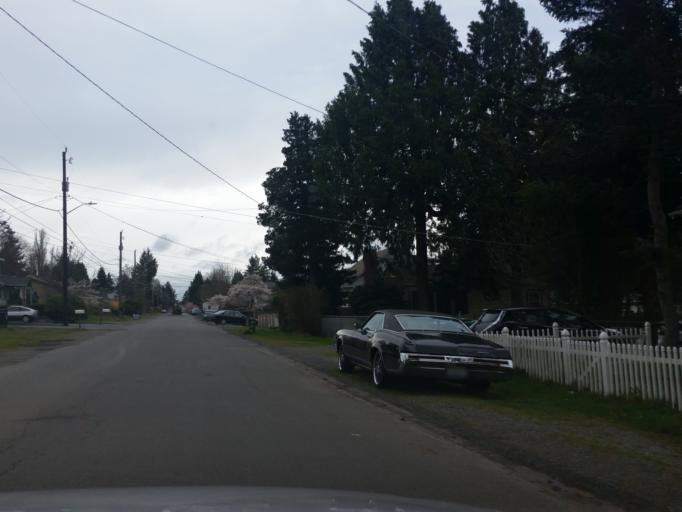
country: US
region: Washington
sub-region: King County
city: Shoreline
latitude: 47.7145
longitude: -122.3502
